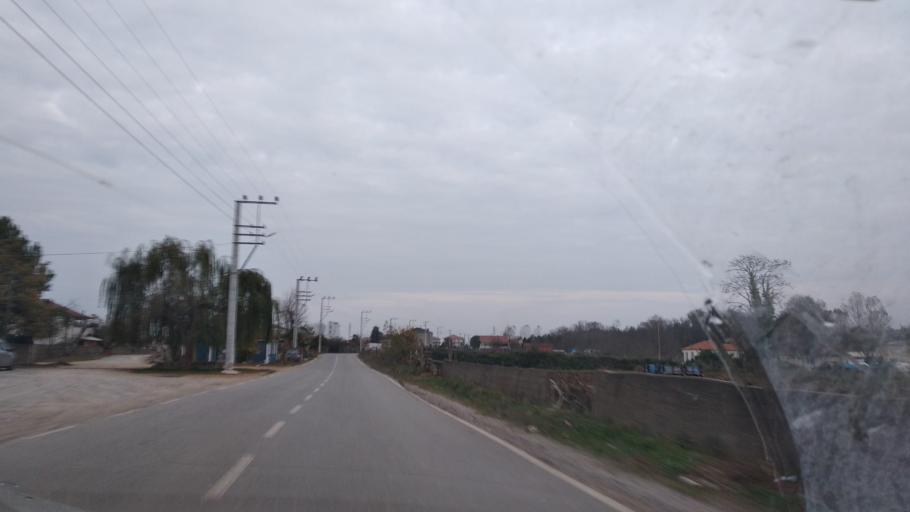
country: TR
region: Sakarya
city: Karasu
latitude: 41.0886
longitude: 30.7137
